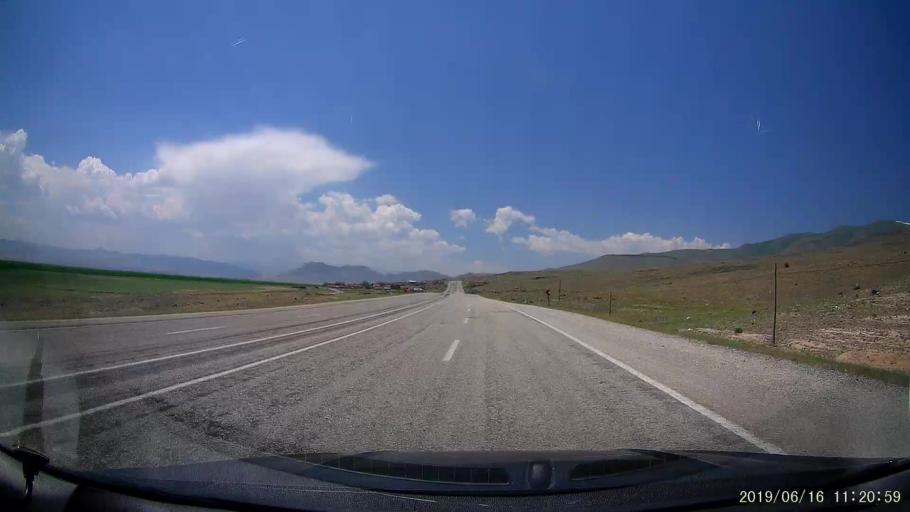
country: TR
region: Agri
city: Dogubayazit
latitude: 39.6979
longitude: 44.0784
